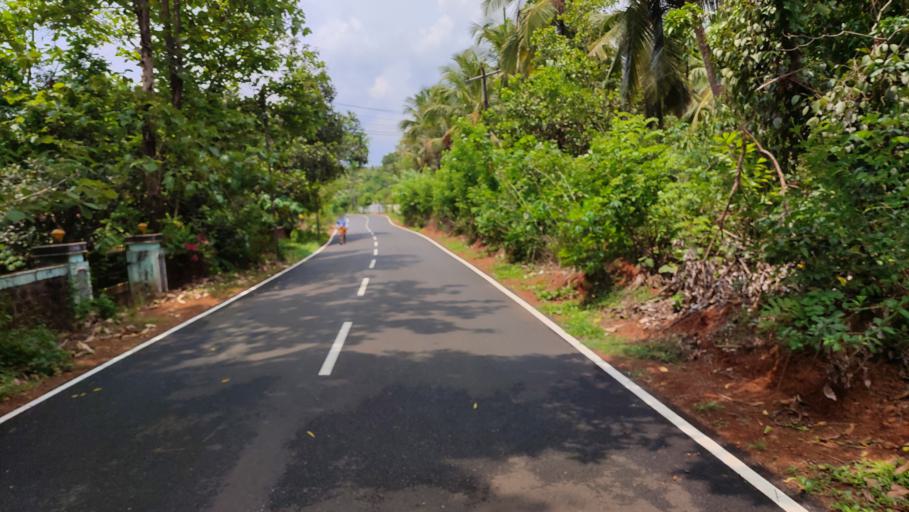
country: IN
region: Kerala
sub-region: Kasaragod District
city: Kannangad
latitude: 12.3190
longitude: 75.1215
